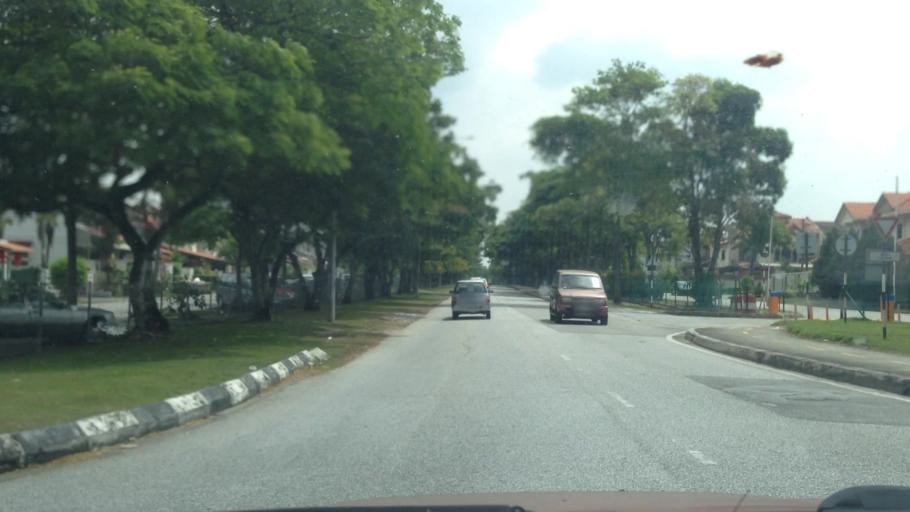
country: MY
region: Selangor
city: Subang Jaya
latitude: 3.0486
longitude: 101.5739
